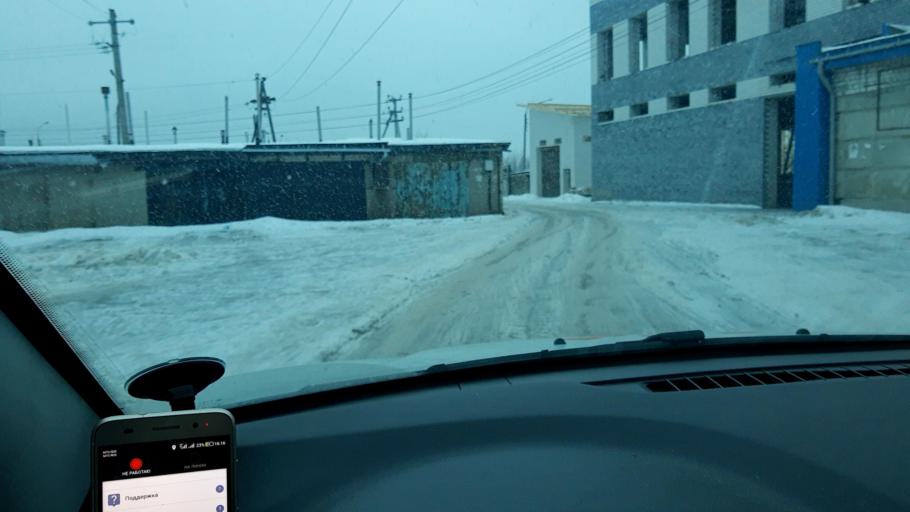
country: RU
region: Nizjnij Novgorod
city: Gorbatovka
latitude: 56.2533
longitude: 43.8326
